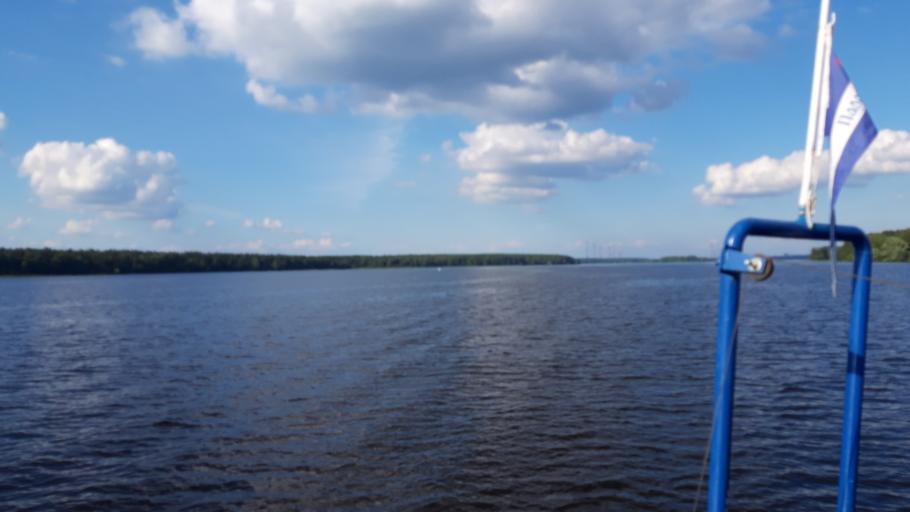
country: RU
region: Tverskaya
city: Konakovo
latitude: 56.6873
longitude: 36.6895
